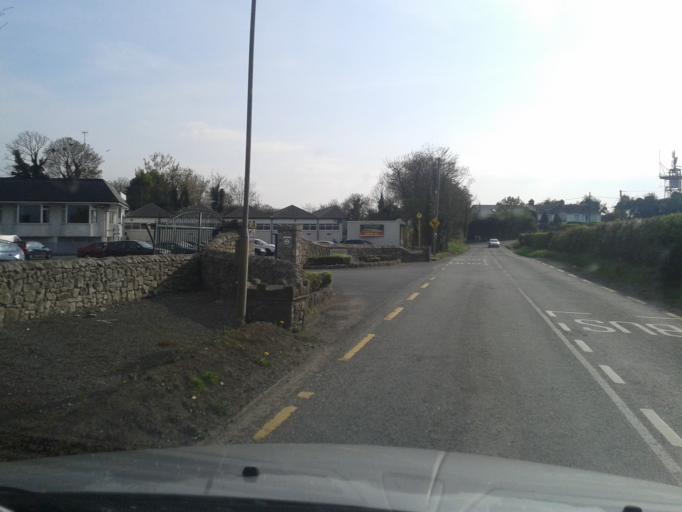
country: IE
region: Leinster
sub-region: Fingal County
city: Swords
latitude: 53.4403
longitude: -6.2494
